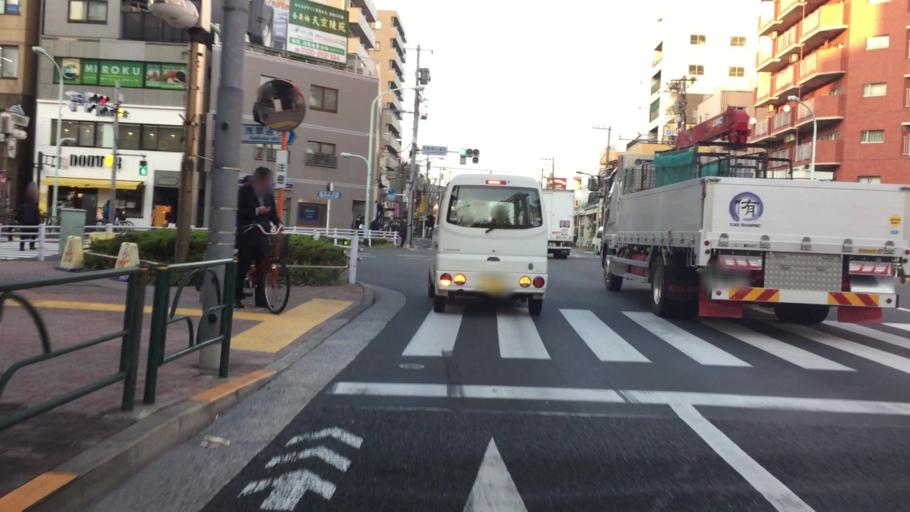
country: JP
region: Tokyo
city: Urayasu
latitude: 35.7084
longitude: 139.8043
